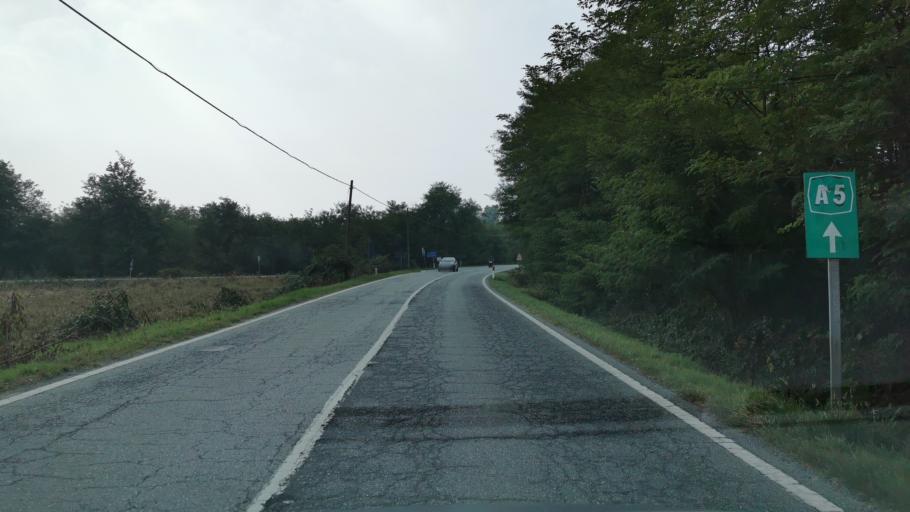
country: IT
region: Piedmont
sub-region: Provincia di Torino
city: Foglizzo
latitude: 45.2501
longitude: 7.8098
